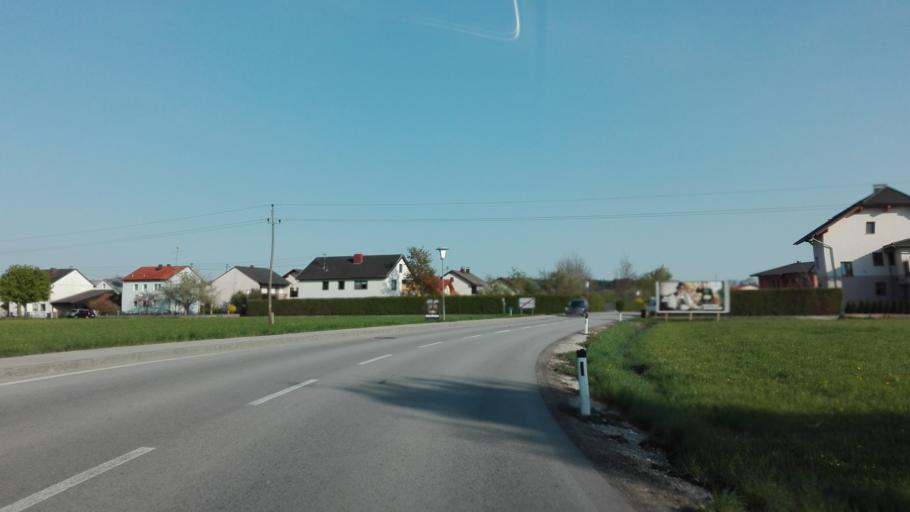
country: AT
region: Upper Austria
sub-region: Politischer Bezirk Grieskirchen
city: Grieskirchen
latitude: 48.3359
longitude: 13.8471
